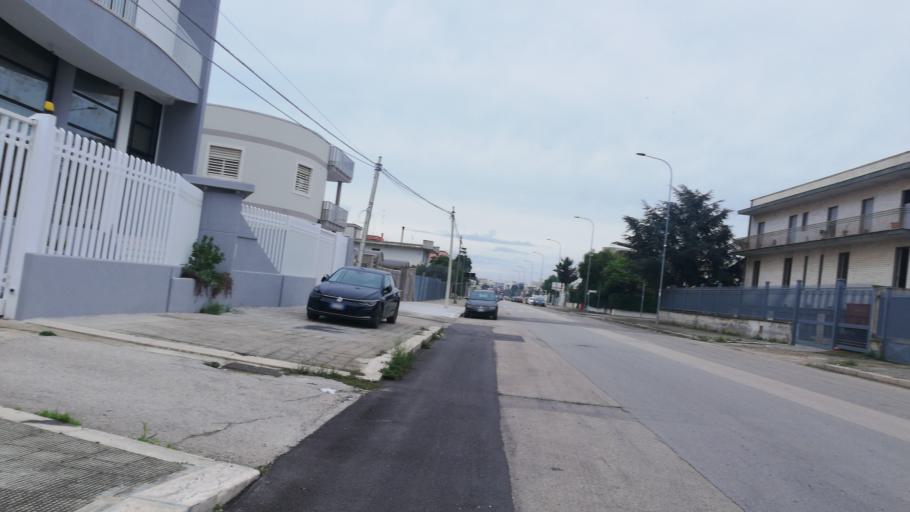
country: IT
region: Apulia
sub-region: Provincia di Bari
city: Bitonto
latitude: 41.1180
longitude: 16.6783
